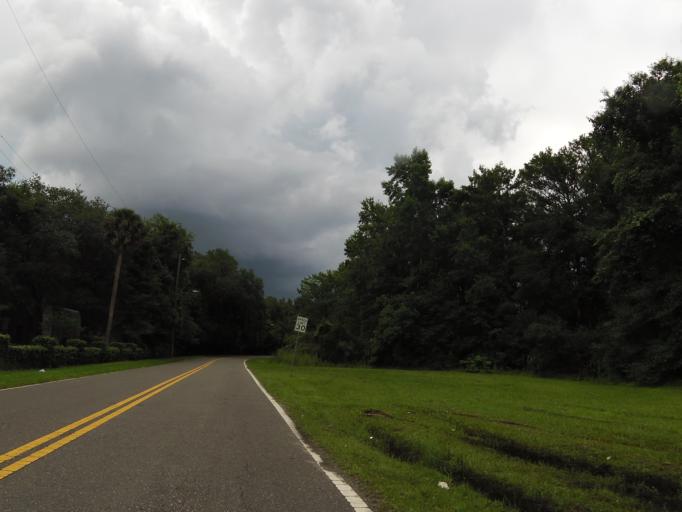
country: US
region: Florida
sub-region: Duval County
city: Jacksonville
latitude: 30.3656
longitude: -81.6432
